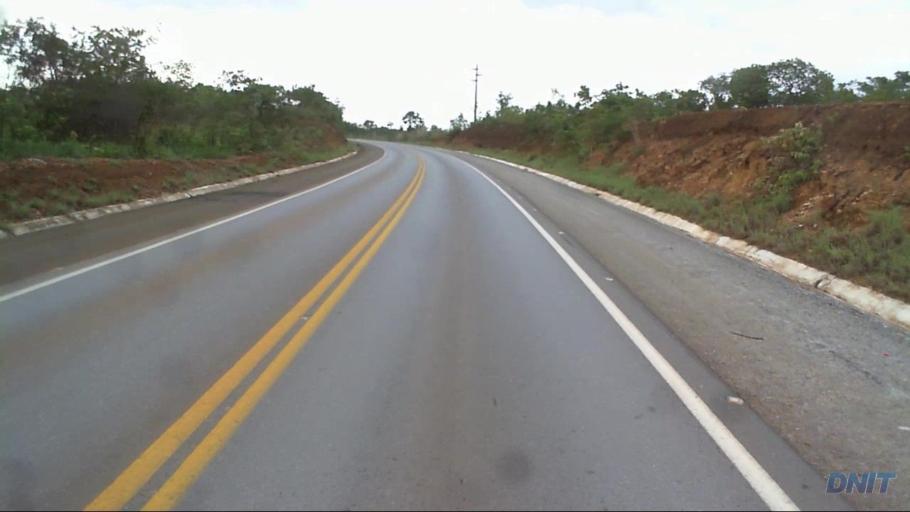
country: BR
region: Goias
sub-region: Barro Alto
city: Barro Alto
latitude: -14.7766
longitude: -49.0571
